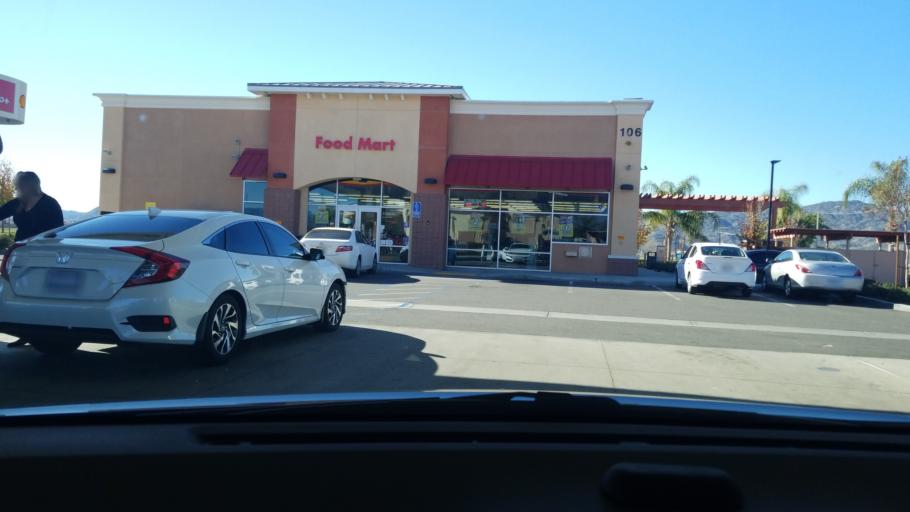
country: US
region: California
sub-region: Riverside County
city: San Jacinto
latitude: 33.7869
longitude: -117.0083
